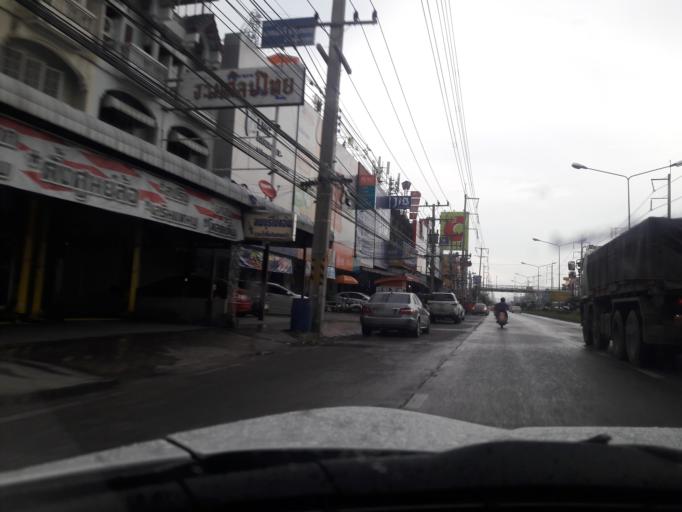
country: TH
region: Lop Buri
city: Lop Buri
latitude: 14.7934
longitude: 100.6697
